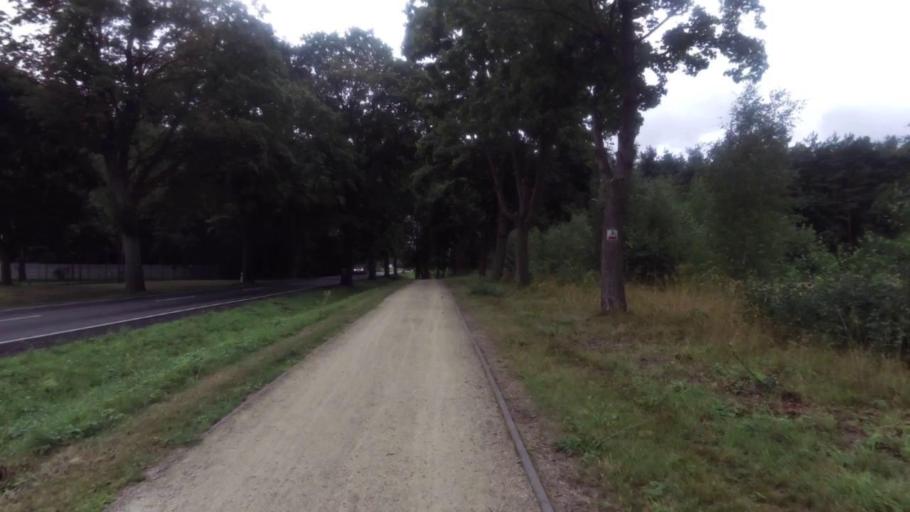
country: PL
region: West Pomeranian Voivodeship
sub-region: Powiat mysliborski
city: Debno
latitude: 52.7222
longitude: 14.6935
